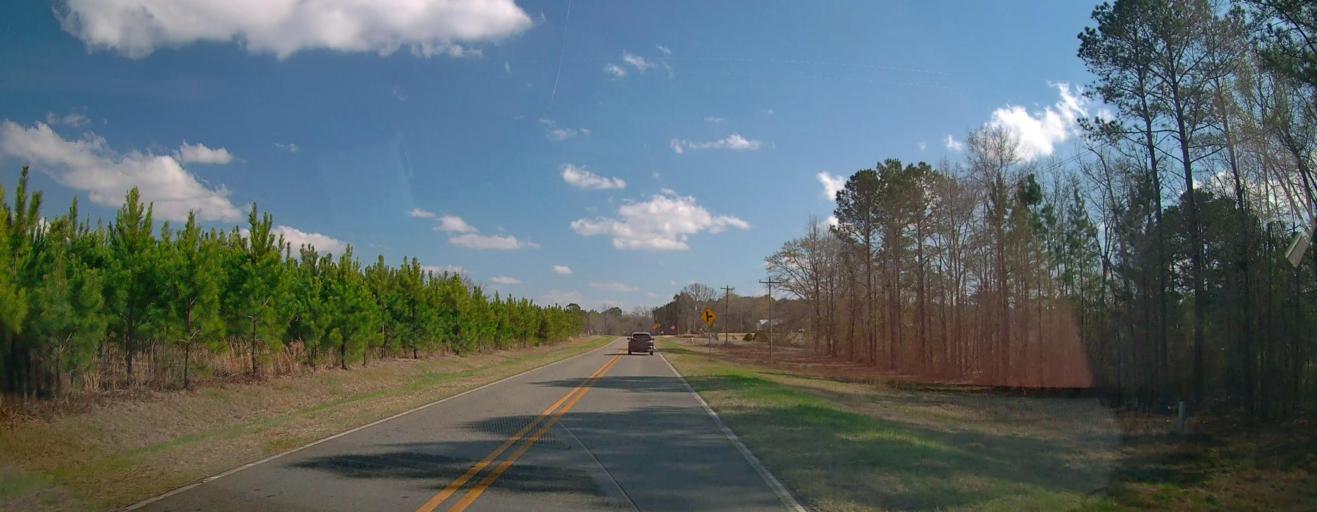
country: US
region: Georgia
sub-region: Laurens County
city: Dublin
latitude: 32.5998
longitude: -83.0728
